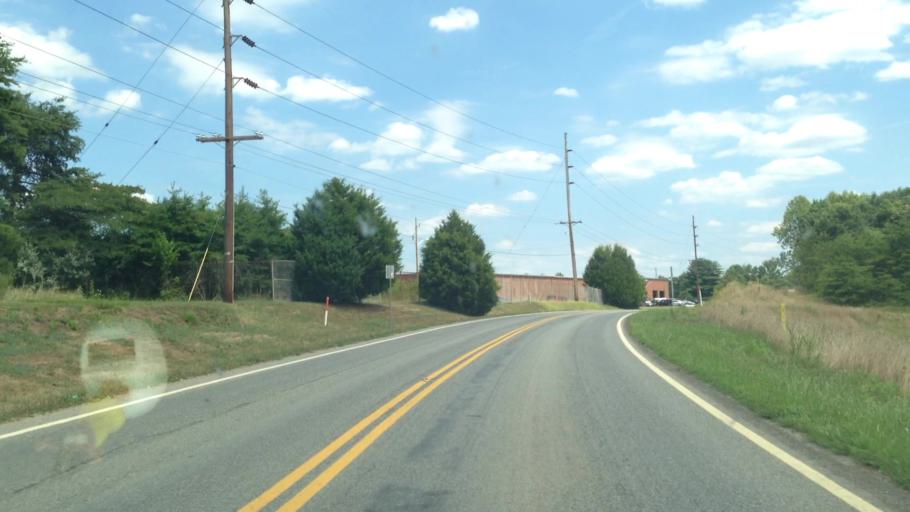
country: US
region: Virginia
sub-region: Henry County
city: Chatmoss
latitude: 36.6273
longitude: -79.8559
